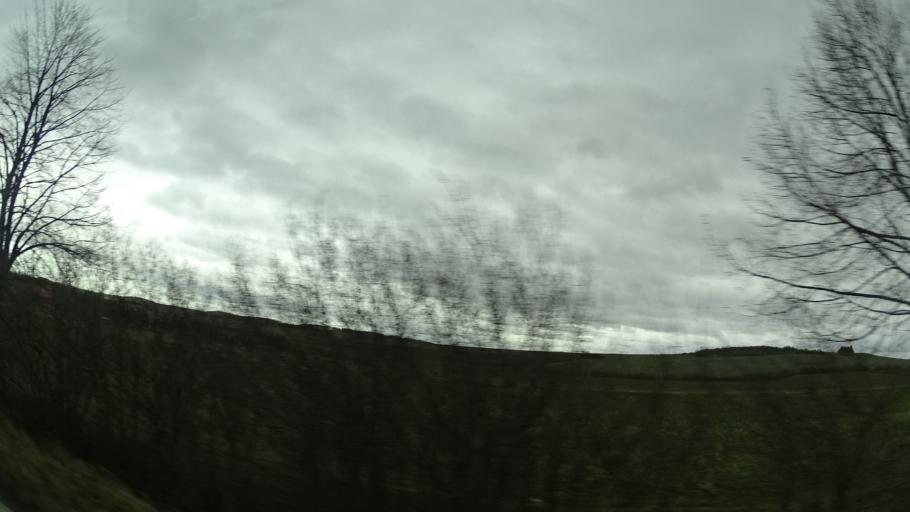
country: DE
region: Thuringia
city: Mechelroda
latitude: 50.8763
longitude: 11.3978
